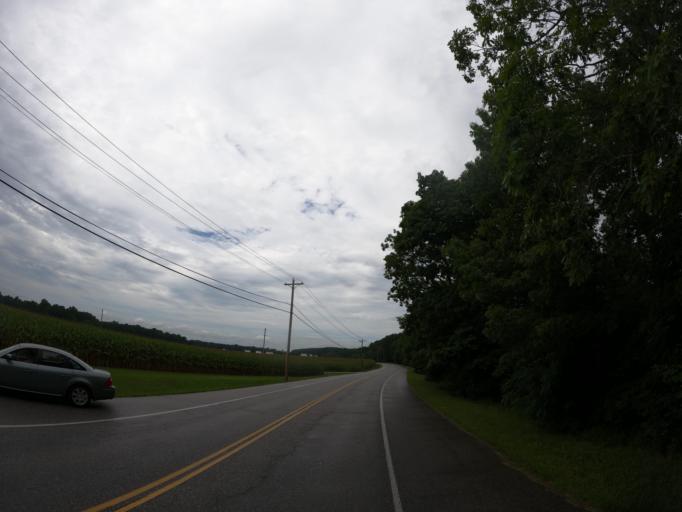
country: US
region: Maryland
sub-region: Saint Mary's County
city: California
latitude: 38.2641
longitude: -76.5265
